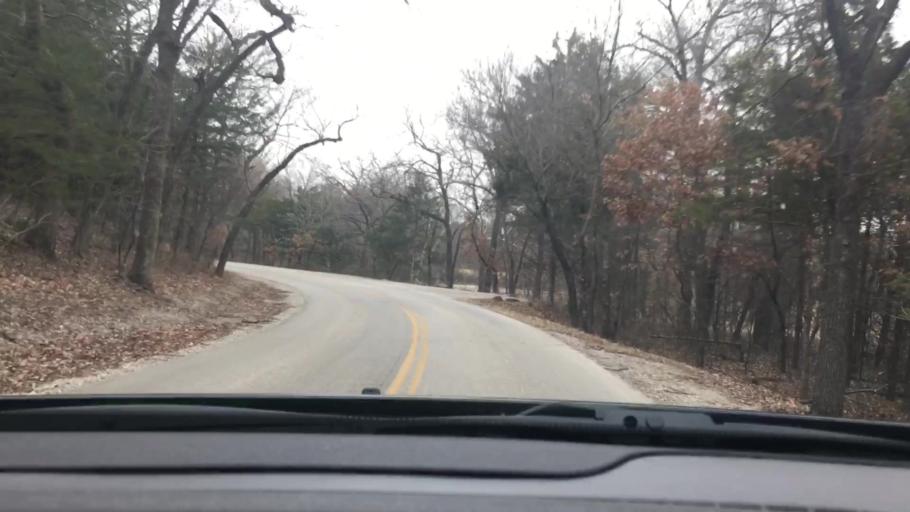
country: US
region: Oklahoma
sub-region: Murray County
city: Sulphur
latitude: 34.5043
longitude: -96.9674
